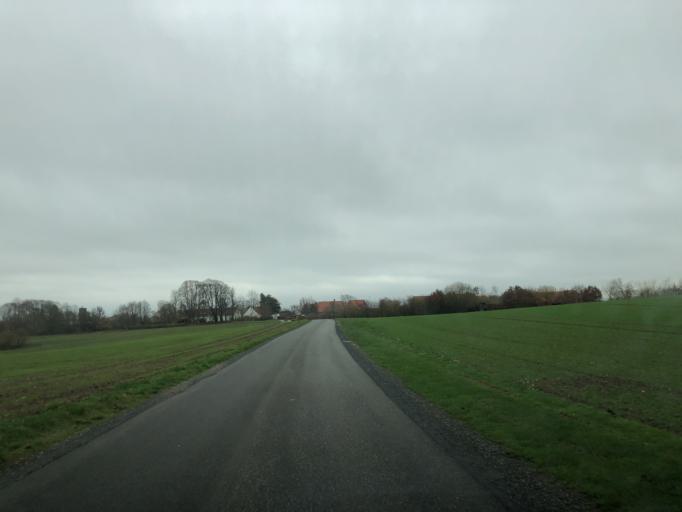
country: DK
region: Central Jutland
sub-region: Skanderborg Kommune
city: Ry
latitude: 56.0738
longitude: 9.8368
